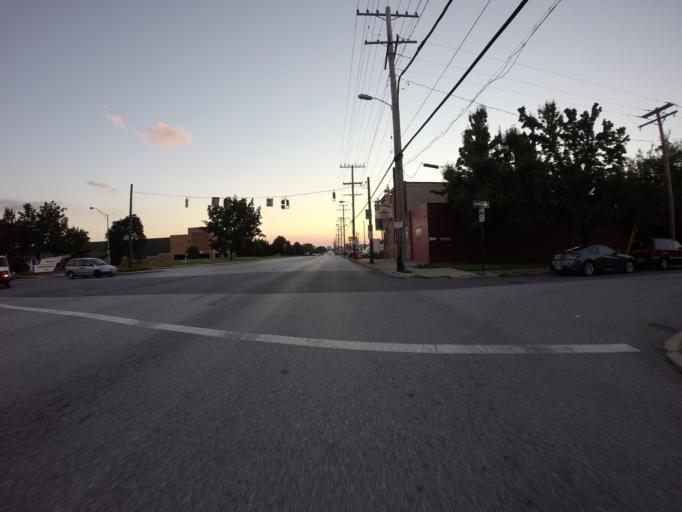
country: US
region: Maryland
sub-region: Baltimore County
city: Dundalk
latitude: 39.2724
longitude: -76.5358
